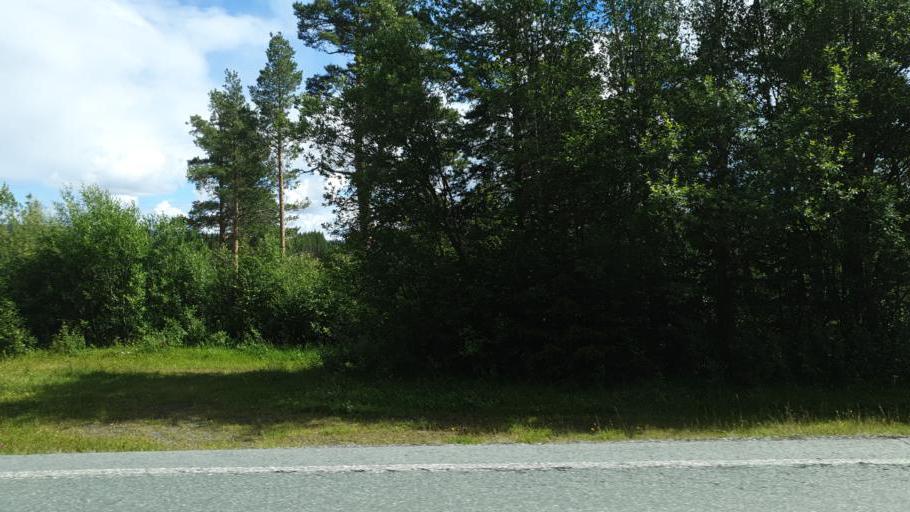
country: NO
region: Sor-Trondelag
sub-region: Rennebu
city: Berkak
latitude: 62.7128
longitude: 9.9596
